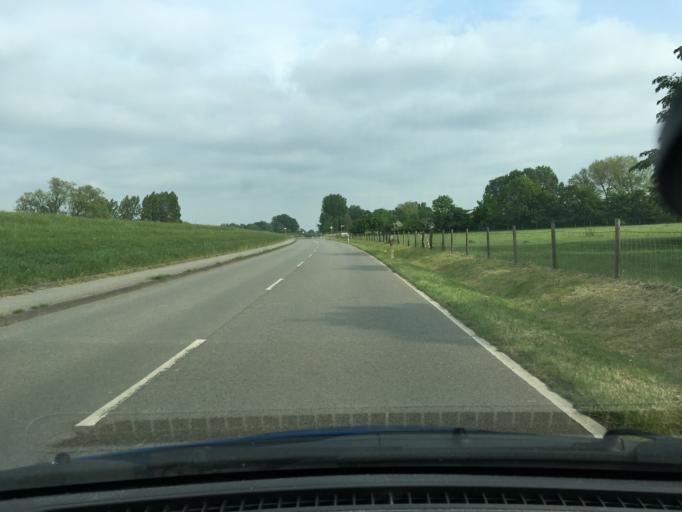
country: DE
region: Hamburg
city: Rothenburgsort
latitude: 53.4822
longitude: 10.0514
